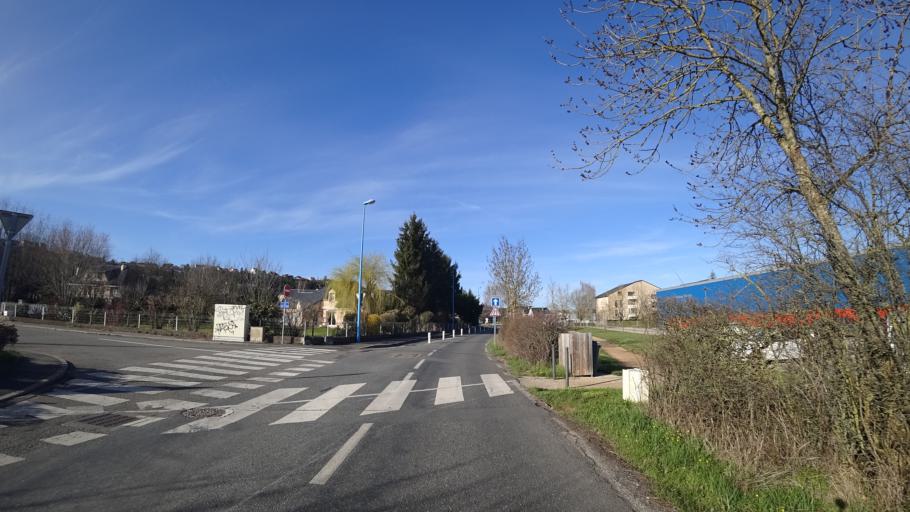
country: FR
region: Midi-Pyrenees
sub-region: Departement de l'Aveyron
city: Rodez
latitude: 44.3718
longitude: 2.5765
